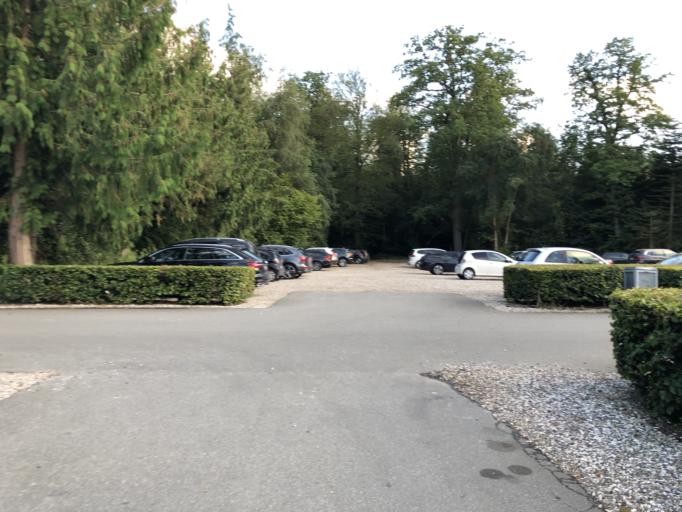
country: DK
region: South Denmark
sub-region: Vejle Kommune
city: Borkop
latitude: 55.6864
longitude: 9.6150
